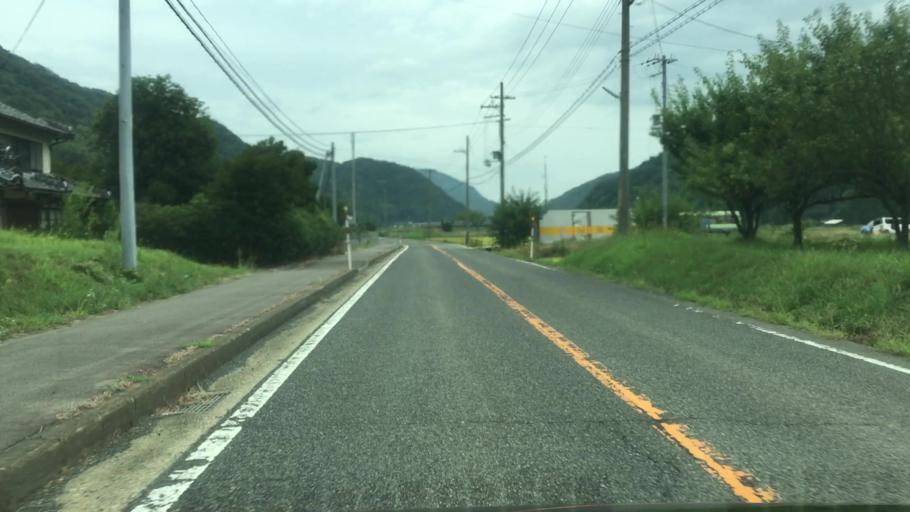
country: JP
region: Hyogo
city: Toyooka
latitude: 35.6315
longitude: 134.6802
